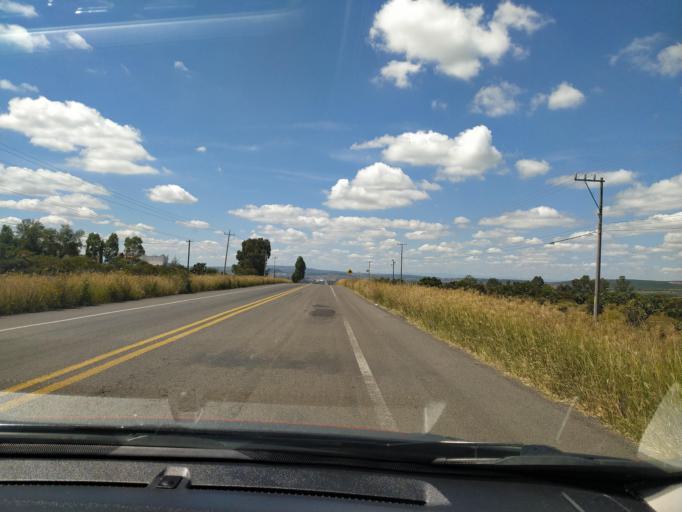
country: MX
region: Jalisco
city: San Miguel el Alto
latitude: 21.0152
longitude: -102.3252
